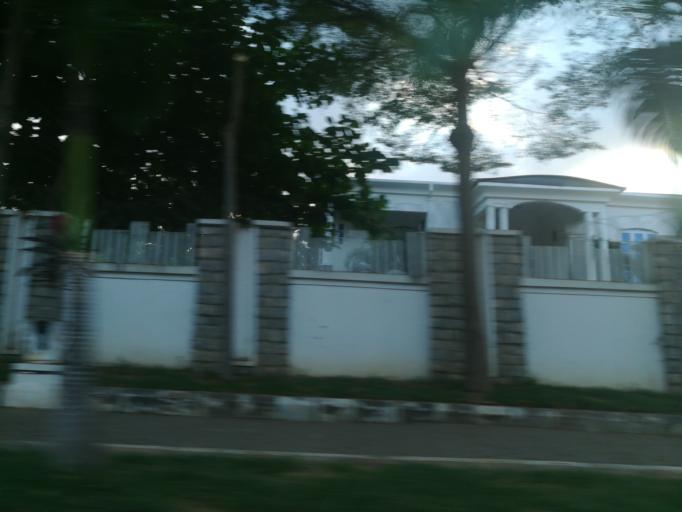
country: NG
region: Abuja Federal Capital Territory
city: Abuja
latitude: 9.0689
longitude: 7.4121
